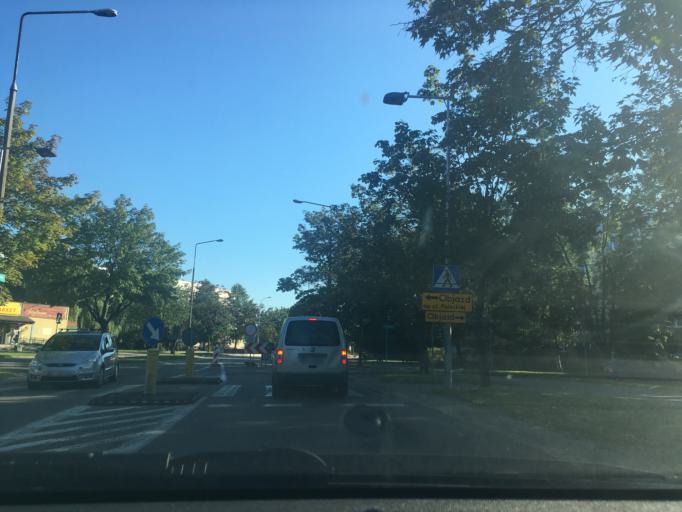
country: PL
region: Podlasie
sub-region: Bialystok
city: Bialystok
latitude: 53.1434
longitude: 23.1488
